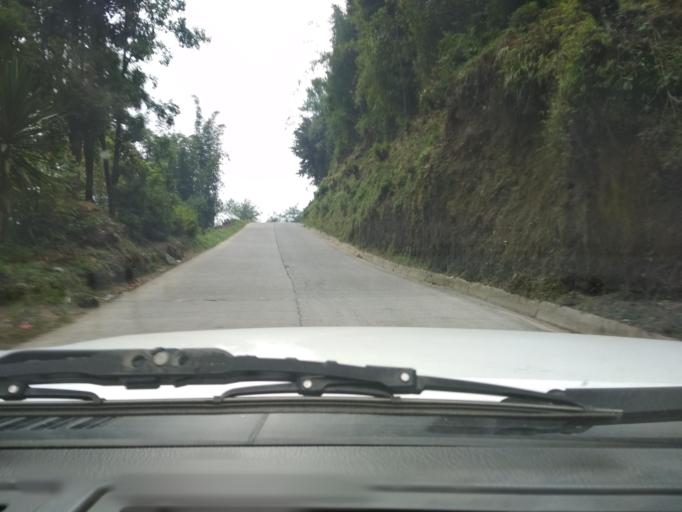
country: MX
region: Veracruz
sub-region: La Perla
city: Barrio de San Miguel
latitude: 18.9353
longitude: -97.1268
